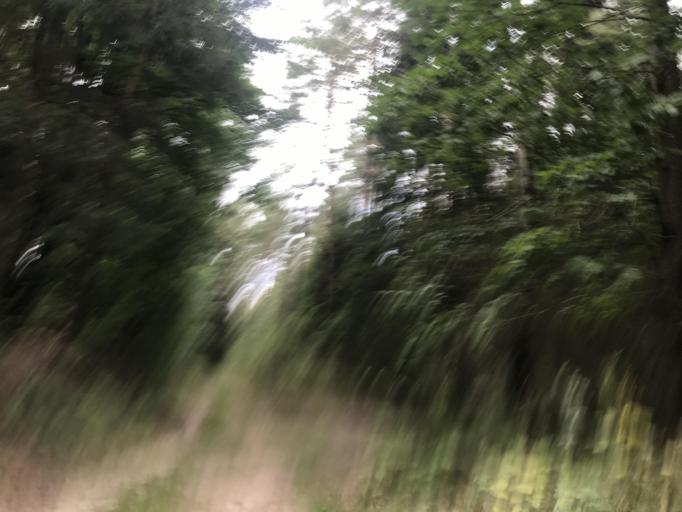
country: DE
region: Lower Saxony
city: Barendorf
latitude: 53.2360
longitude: 10.5400
